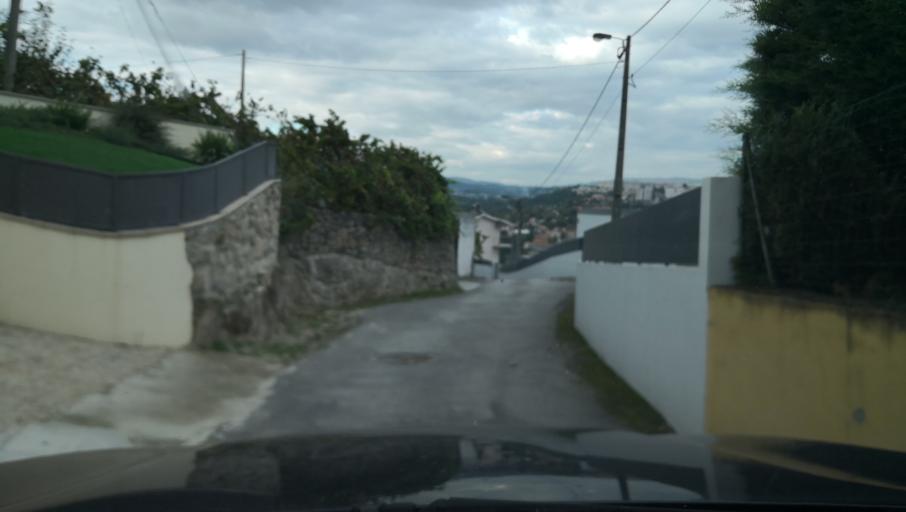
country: PT
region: Vila Real
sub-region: Vila Real
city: Vila Real
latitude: 41.2861
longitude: -7.7634
